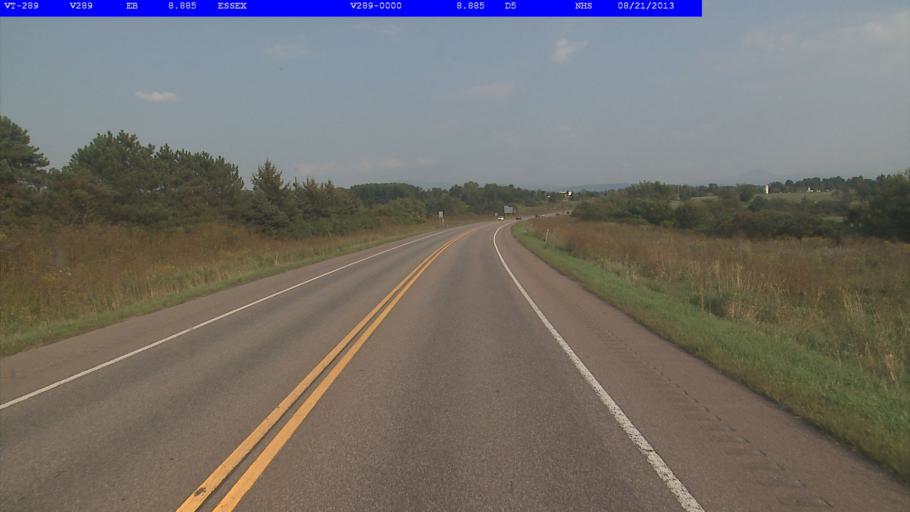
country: US
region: Vermont
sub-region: Chittenden County
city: Essex Junction
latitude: 44.5126
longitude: -73.0969
